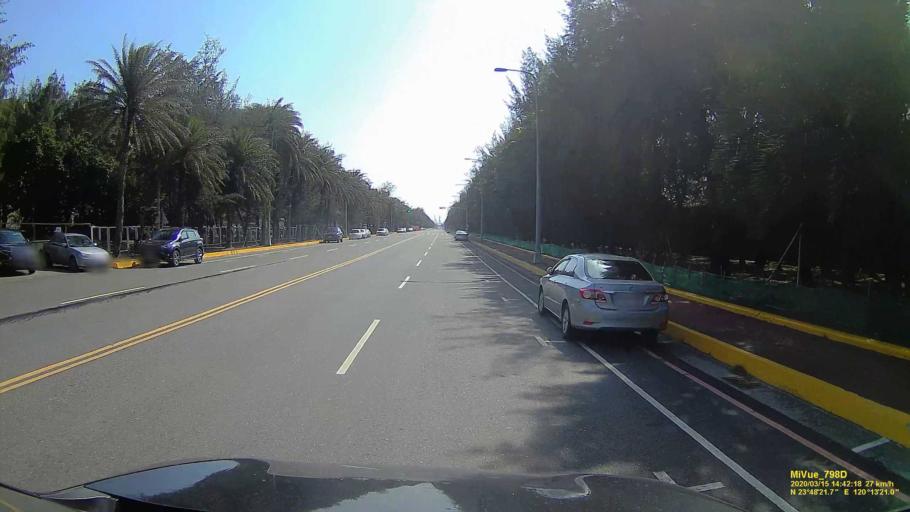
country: TW
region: Taiwan
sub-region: Yunlin
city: Douliu
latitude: 23.8059
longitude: 120.2224
